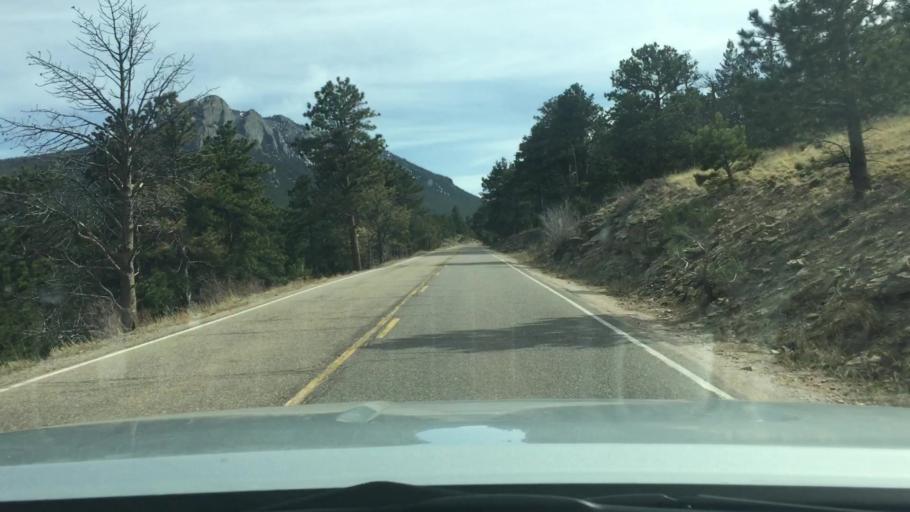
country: US
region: Colorado
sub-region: Larimer County
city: Estes Park
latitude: 40.3300
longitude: -105.5294
